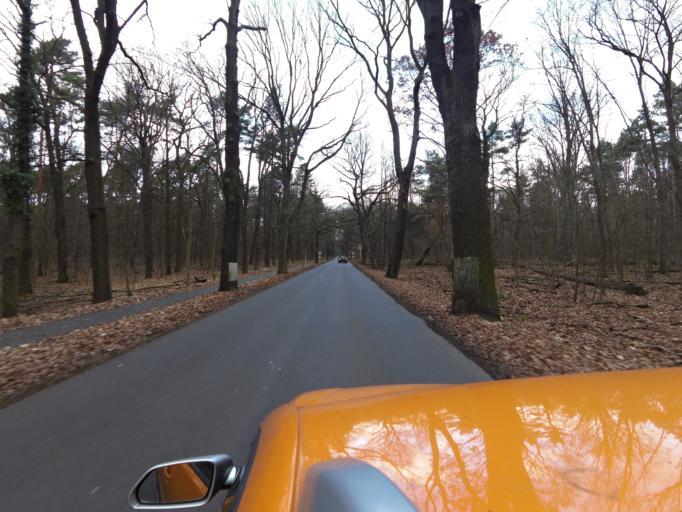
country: DE
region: Berlin
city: Nikolassee
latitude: 52.4419
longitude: 13.1999
